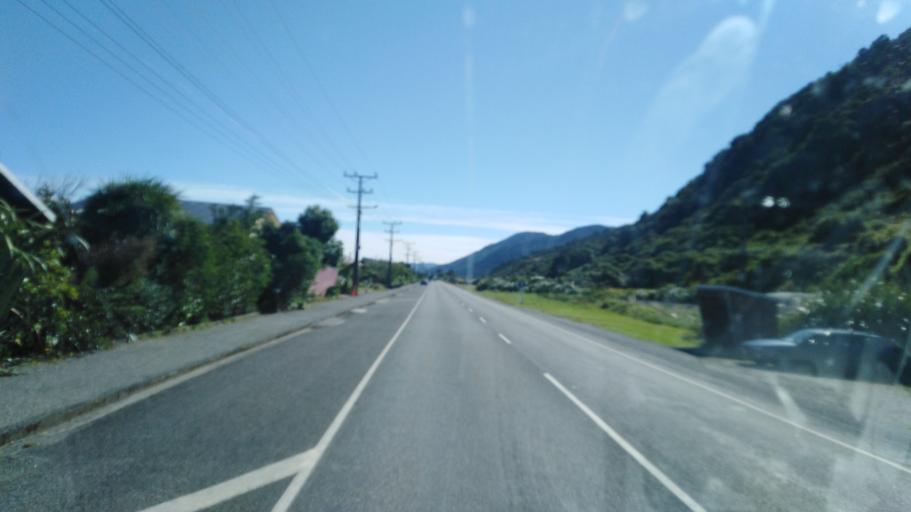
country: NZ
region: West Coast
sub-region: Buller District
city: Westport
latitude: -41.6241
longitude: 171.8590
